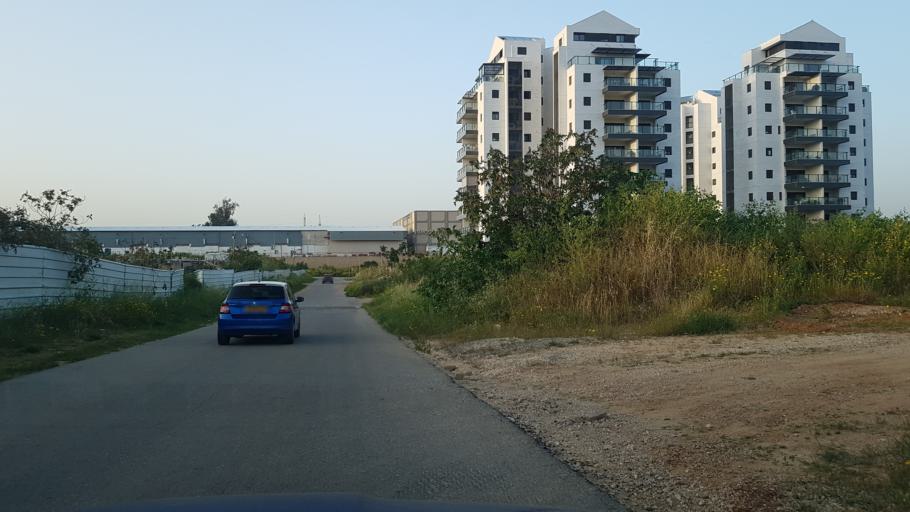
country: IL
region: Central District
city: Ra'anana
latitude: 32.1963
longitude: 34.8885
